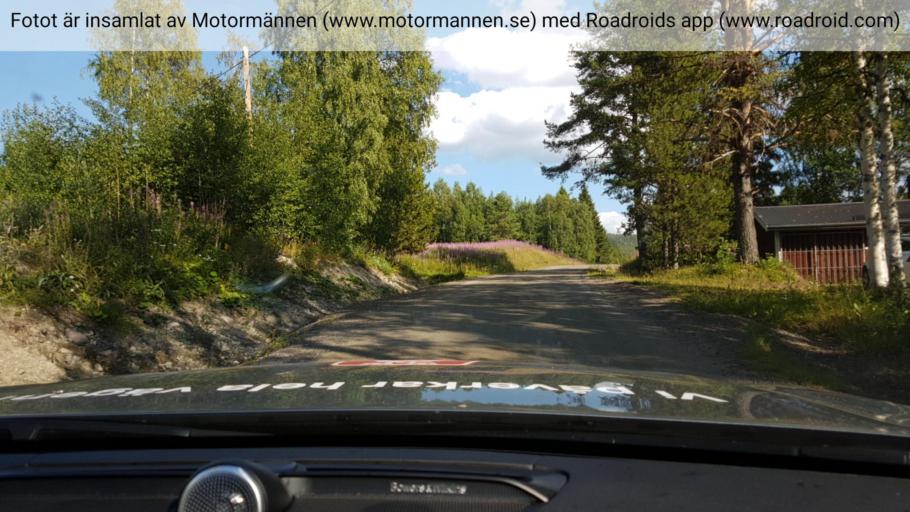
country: SE
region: Jaemtland
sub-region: Stroemsunds Kommun
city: Stroemsund
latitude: 63.9925
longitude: 15.9900
